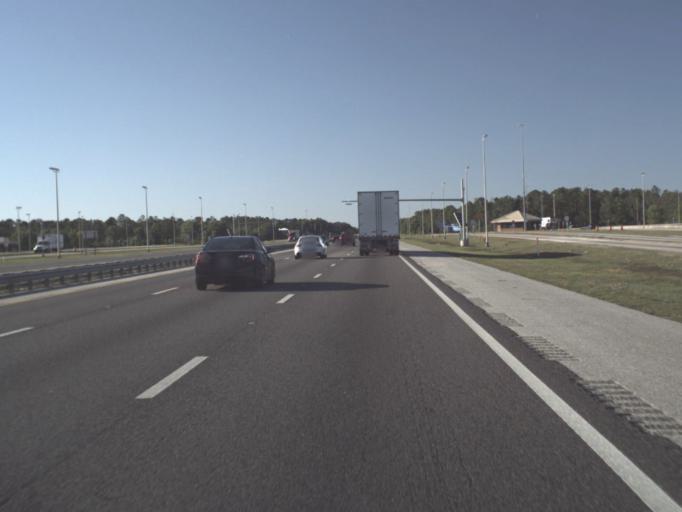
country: US
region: Florida
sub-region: Flagler County
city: Bunnell
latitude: 29.5090
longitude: -81.1962
